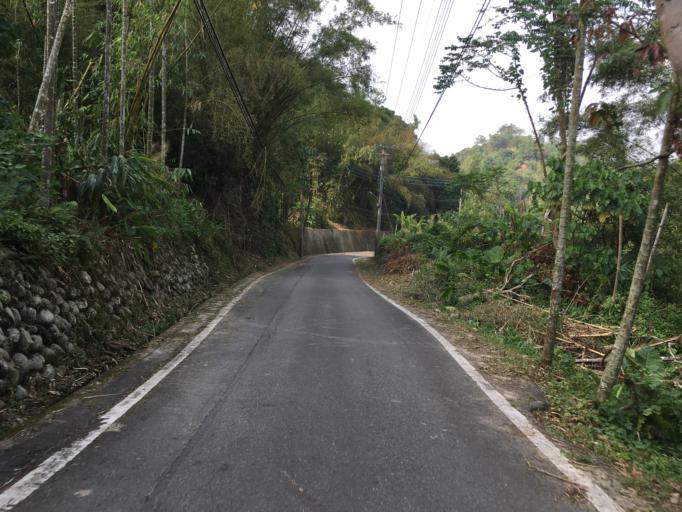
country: TW
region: Taiwan
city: Fengyuan
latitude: 24.1843
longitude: 120.7746
